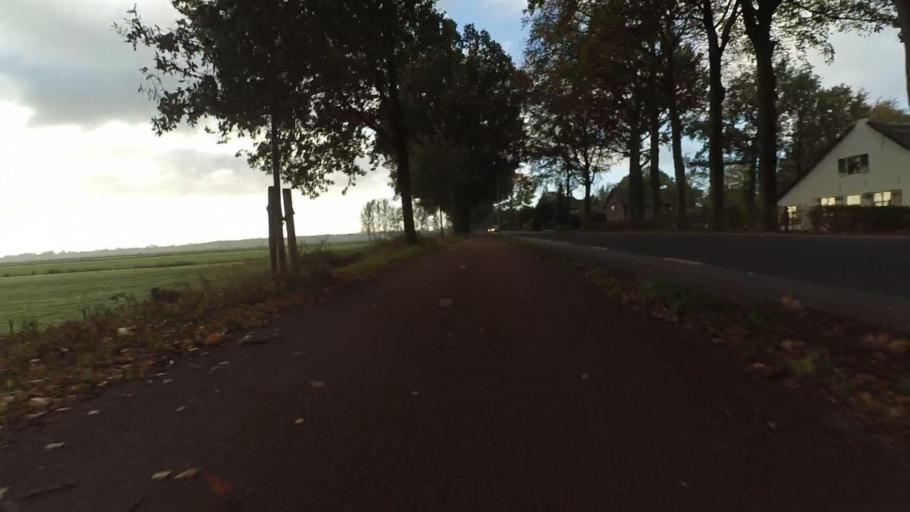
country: NL
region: Utrecht
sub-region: Gemeente Baarn
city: Baarn
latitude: 52.2396
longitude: 5.2618
